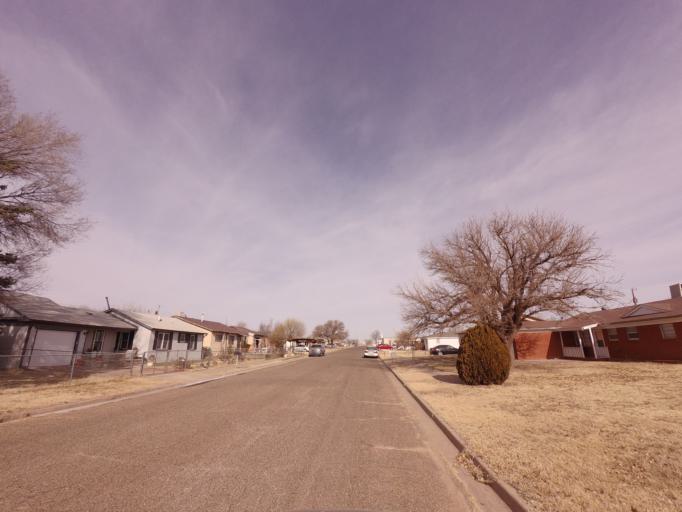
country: US
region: New Mexico
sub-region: Curry County
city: Clovis
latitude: 34.4087
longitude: -103.2363
